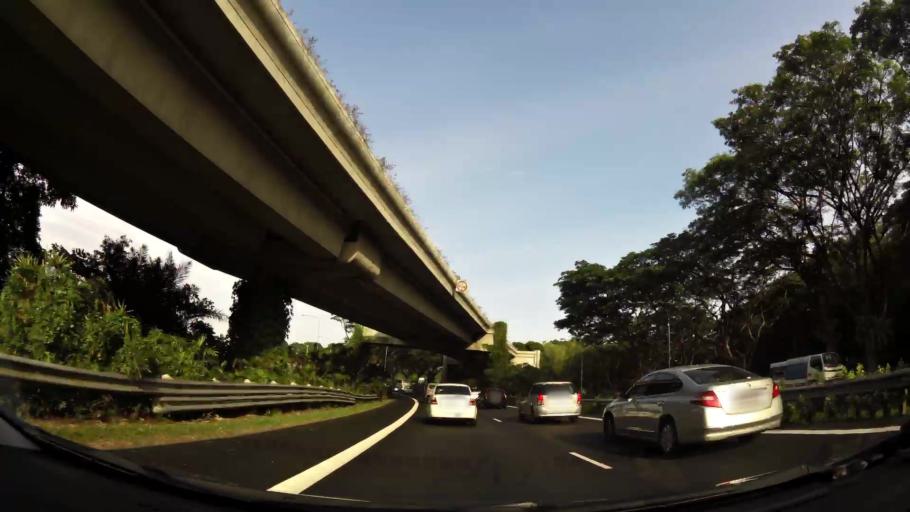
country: MY
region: Johor
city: Johor Bahru
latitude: 1.3617
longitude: 103.7091
